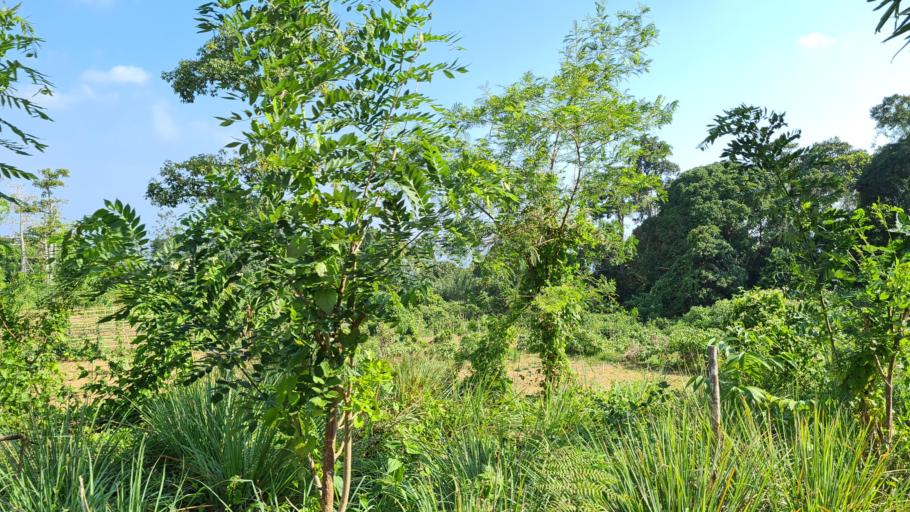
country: ID
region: Lampung
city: Kuripan
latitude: -5.0691
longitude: 103.8672
